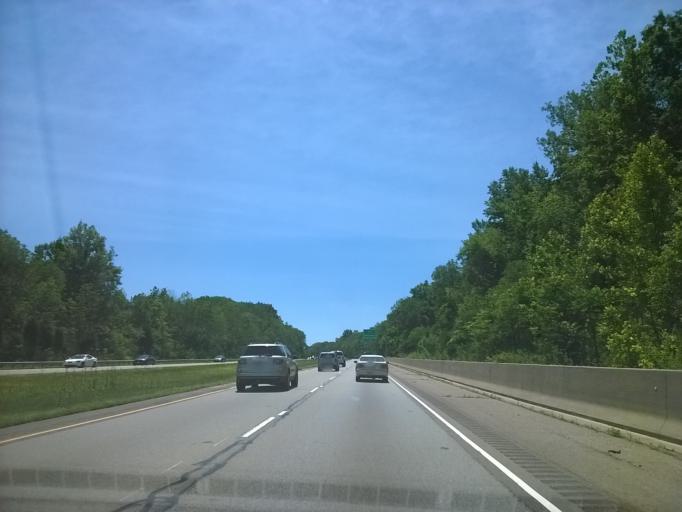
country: US
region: Ohio
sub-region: Hamilton County
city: Grandview
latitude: 39.2338
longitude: -84.7603
